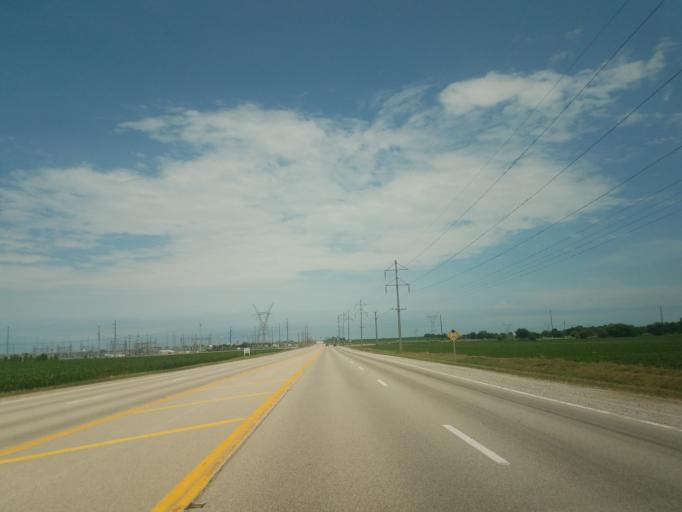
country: US
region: Illinois
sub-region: McLean County
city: Downs
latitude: 40.4475
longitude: -88.9017
